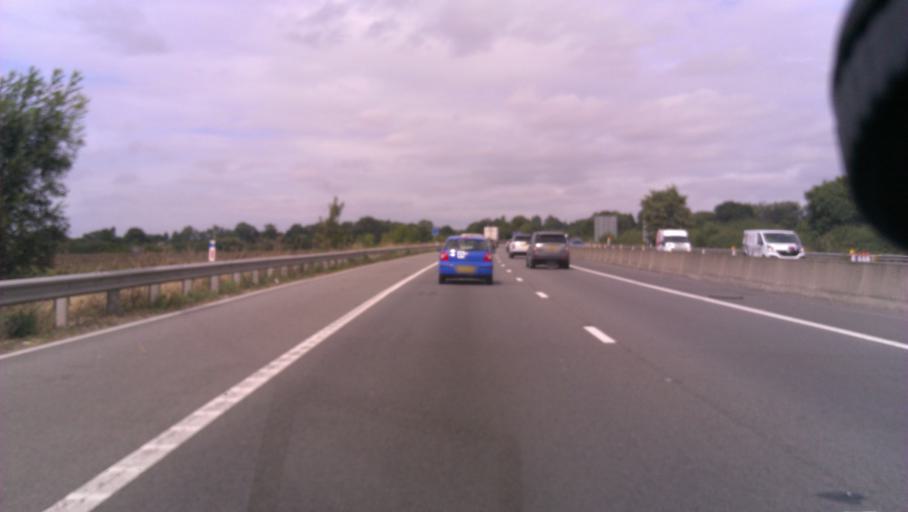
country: GB
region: England
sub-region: Essex
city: Stansted
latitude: 51.8859
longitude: 0.2065
